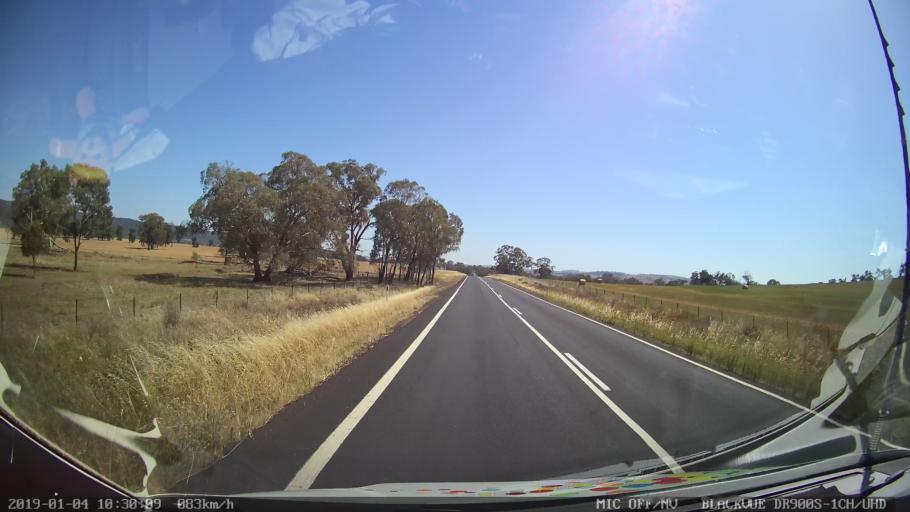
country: AU
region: New South Wales
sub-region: Cabonne
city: Canowindra
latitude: -33.3490
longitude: 148.6262
